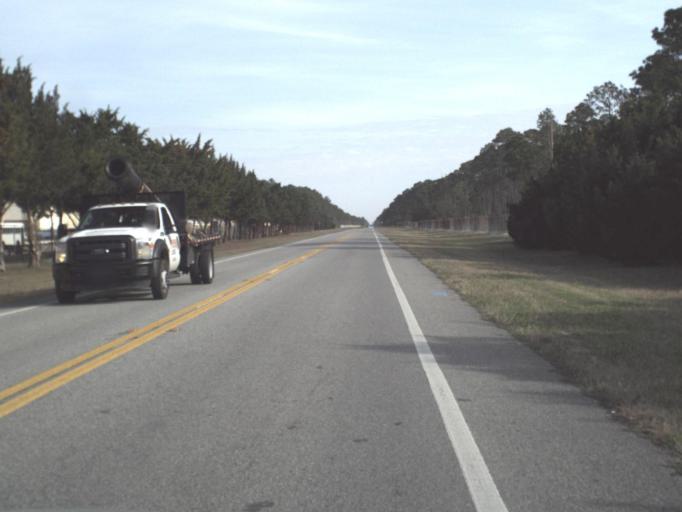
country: US
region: Florida
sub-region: Bay County
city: Tyndall Air Force Base
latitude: 30.0633
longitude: -85.5816
